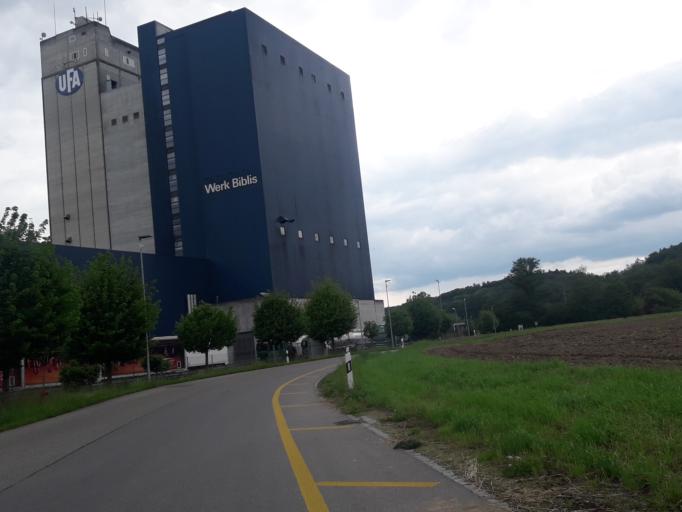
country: CH
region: Bern
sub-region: Oberaargau
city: Herzogenbuchsee
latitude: 47.1948
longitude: 7.6964
